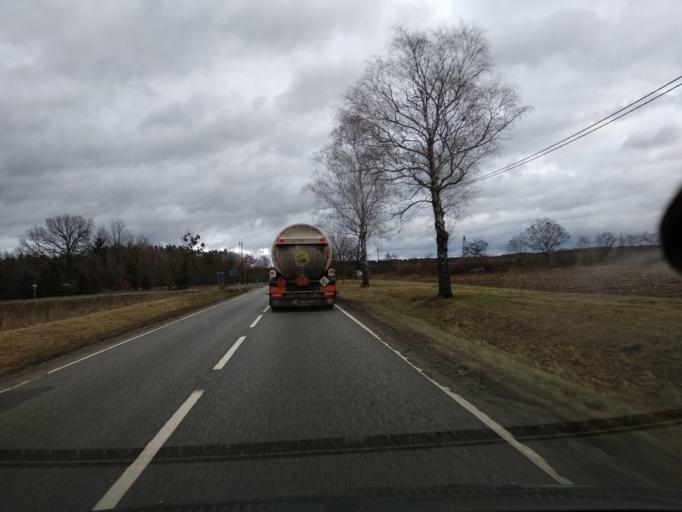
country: PL
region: Lower Silesian Voivodeship
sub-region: Powiat olesnicki
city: Twardogora
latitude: 51.2957
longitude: 17.5278
